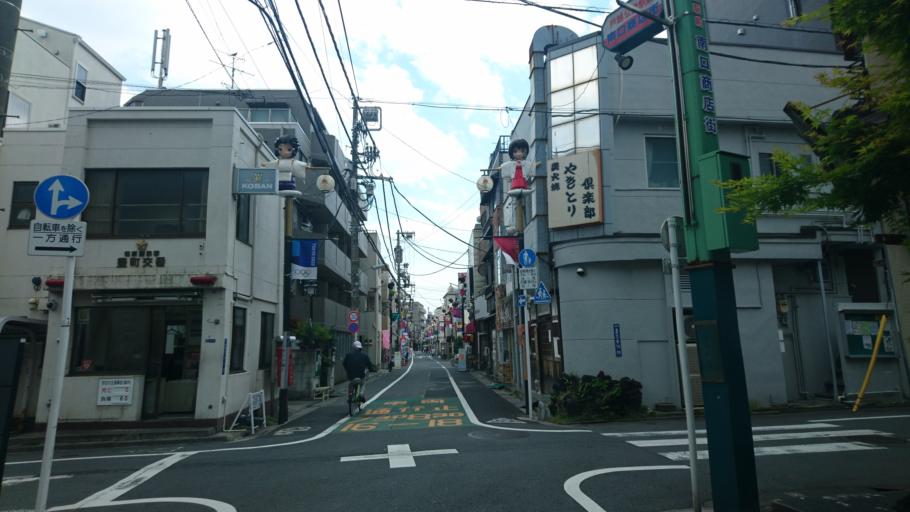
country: JP
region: Kanagawa
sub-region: Kawasaki-shi
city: Kawasaki
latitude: 35.6068
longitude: 139.7180
